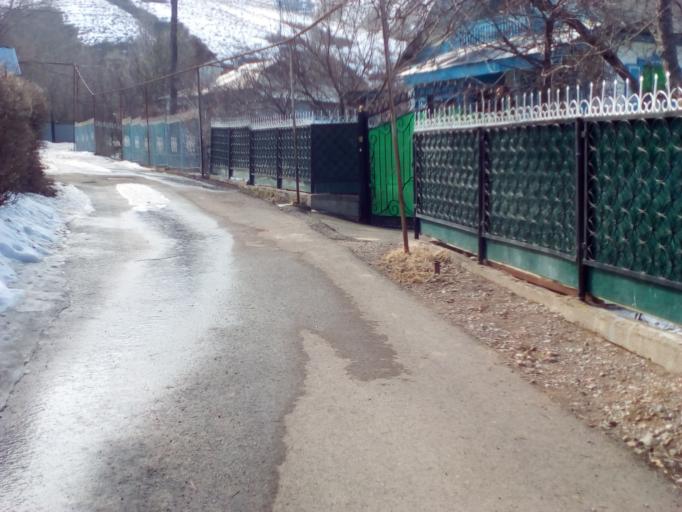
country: KZ
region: Almaty Oblysy
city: Burunday
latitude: 43.1534
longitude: 76.4170
